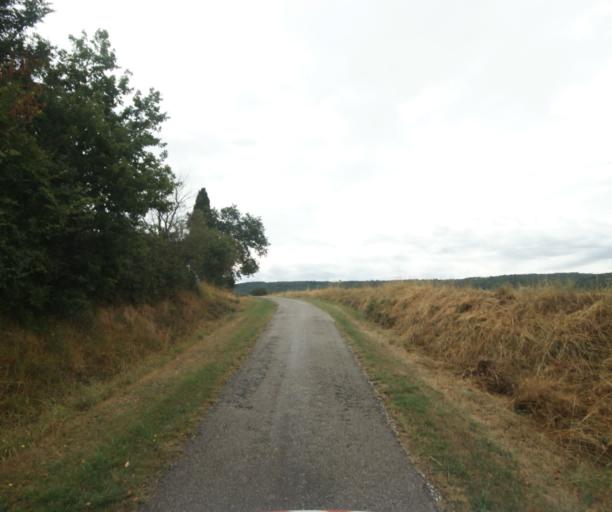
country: FR
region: Midi-Pyrenees
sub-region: Departement de la Haute-Garonne
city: Revel
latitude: 43.4231
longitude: 1.9803
